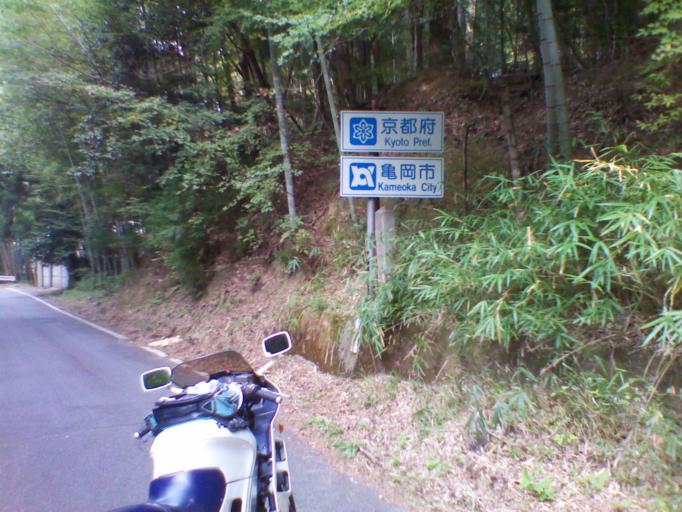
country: JP
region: Kyoto
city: Kameoka
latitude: 34.9170
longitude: 135.5568
